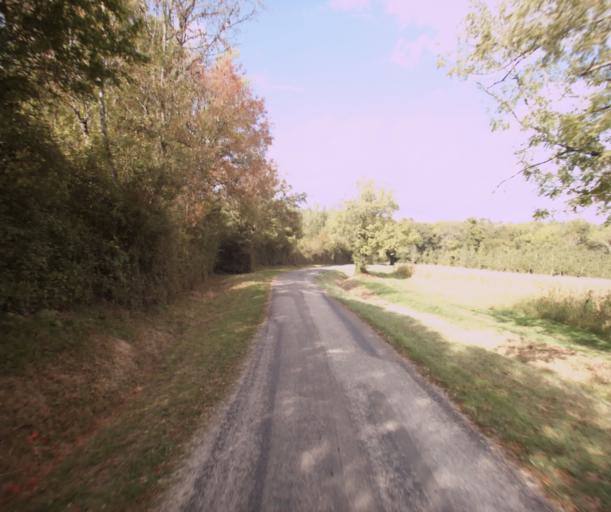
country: FR
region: Midi-Pyrenees
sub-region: Departement du Gers
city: Cazaubon
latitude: 43.9143
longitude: -0.0508
